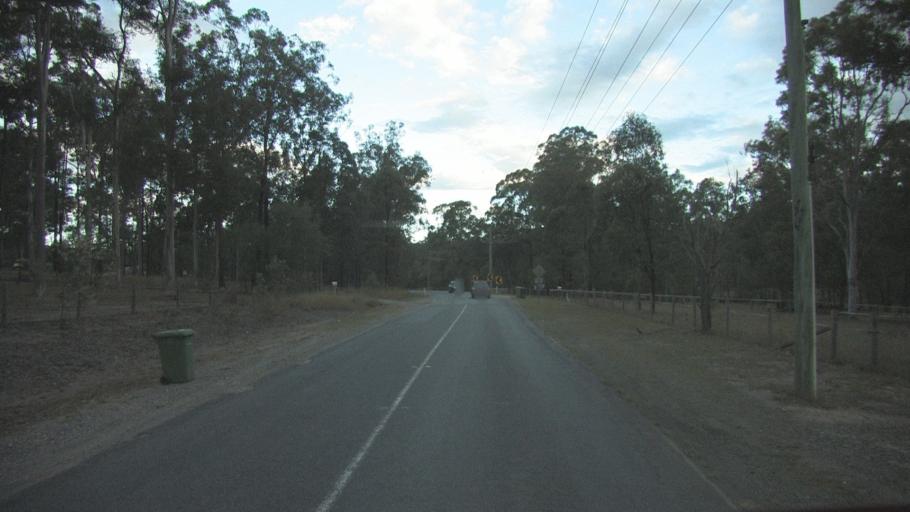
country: AU
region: Queensland
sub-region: Logan
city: Chambers Flat
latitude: -27.7895
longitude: 153.1363
